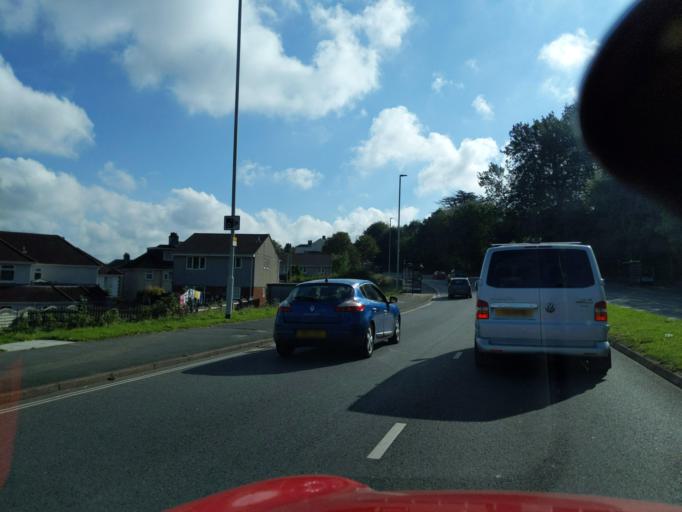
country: GB
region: England
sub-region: Plymouth
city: Plymouth
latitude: 50.3992
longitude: -4.1351
